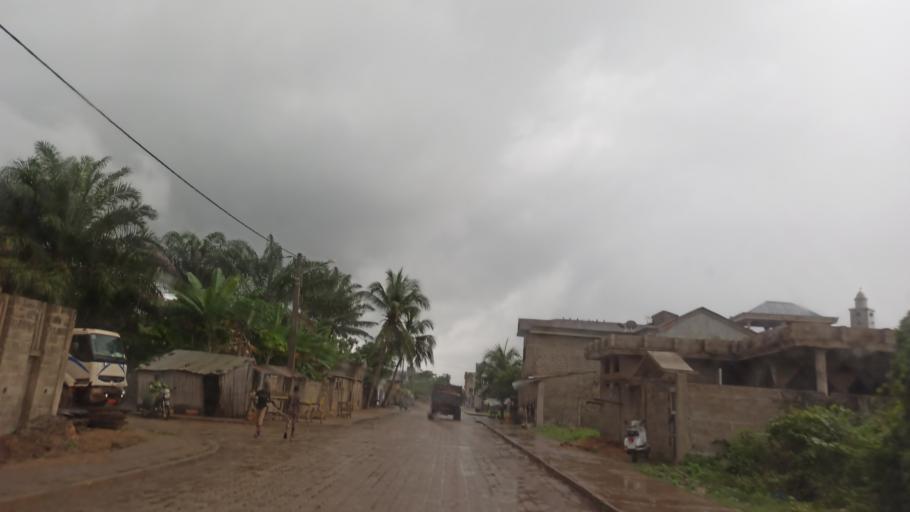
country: BJ
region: Queme
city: Porto-Novo
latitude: 6.4670
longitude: 2.6512
